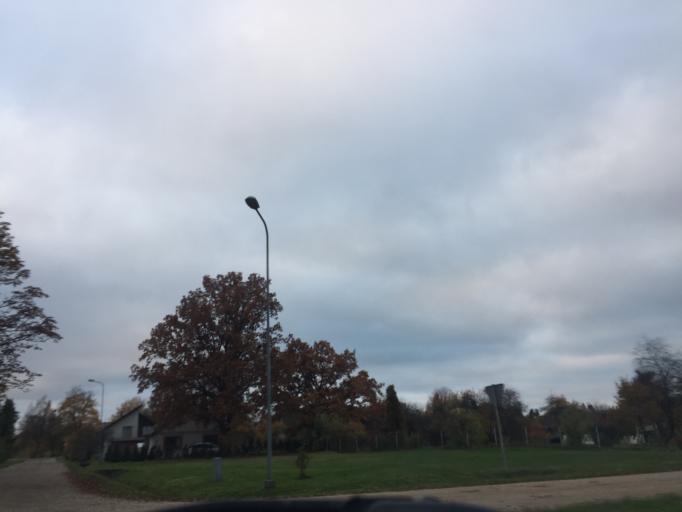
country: LV
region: Skrunda
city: Skrunda
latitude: 56.6780
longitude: 22.0229
